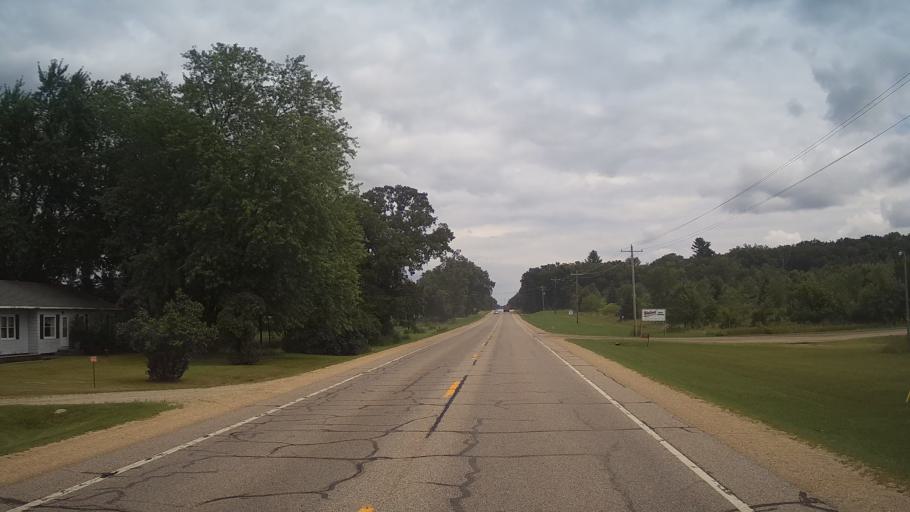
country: US
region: Wisconsin
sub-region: Waushara County
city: Wautoma
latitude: 44.0684
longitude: -89.3247
